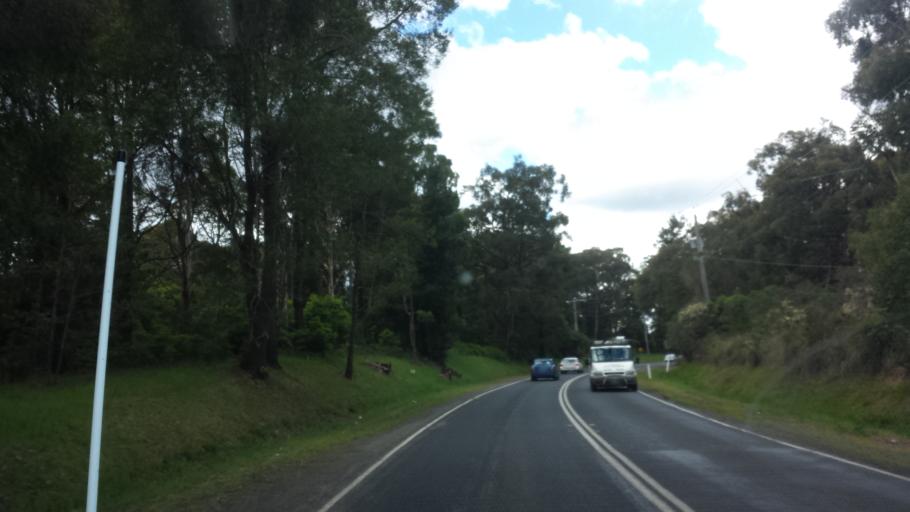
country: AU
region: Victoria
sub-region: Yarra Ranges
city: Selby
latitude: -37.9338
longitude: 145.4095
